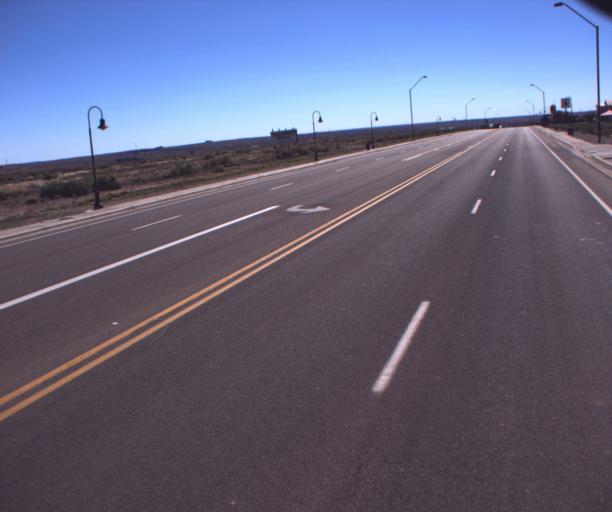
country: US
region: Arizona
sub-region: Navajo County
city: Holbrook
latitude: 34.9228
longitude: -110.1469
